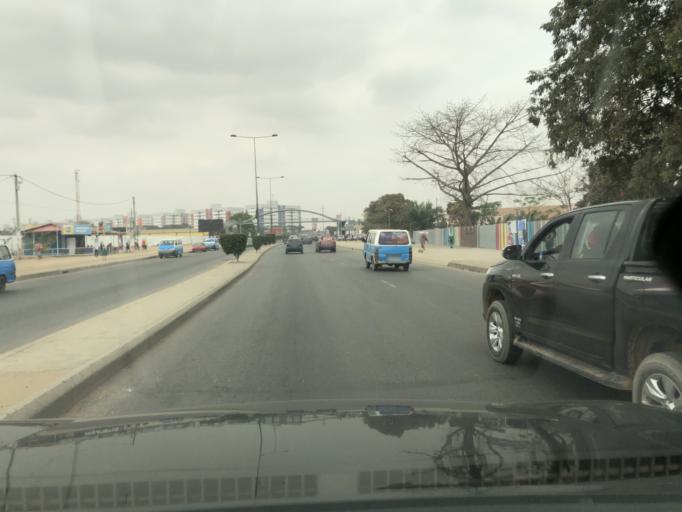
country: AO
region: Luanda
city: Luanda
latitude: -8.8437
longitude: 13.2842
